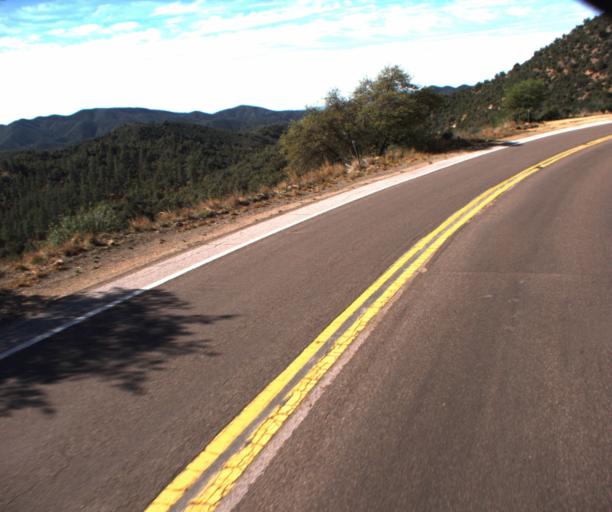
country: US
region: Arizona
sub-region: Yavapai County
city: Prescott
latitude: 34.4543
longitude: -112.5238
